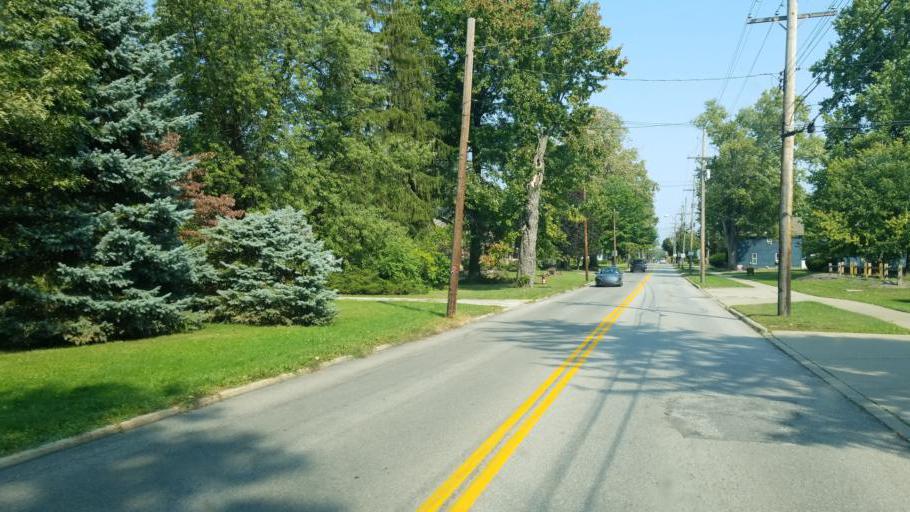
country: US
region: Ohio
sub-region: Lake County
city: Painesville
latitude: 41.7087
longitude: -81.2393
